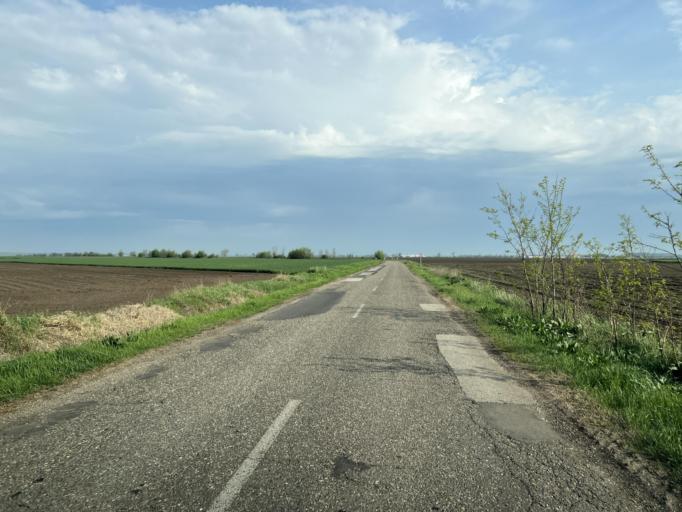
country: HU
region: Pest
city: Tapioszentmarton
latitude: 47.2864
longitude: 19.7630
